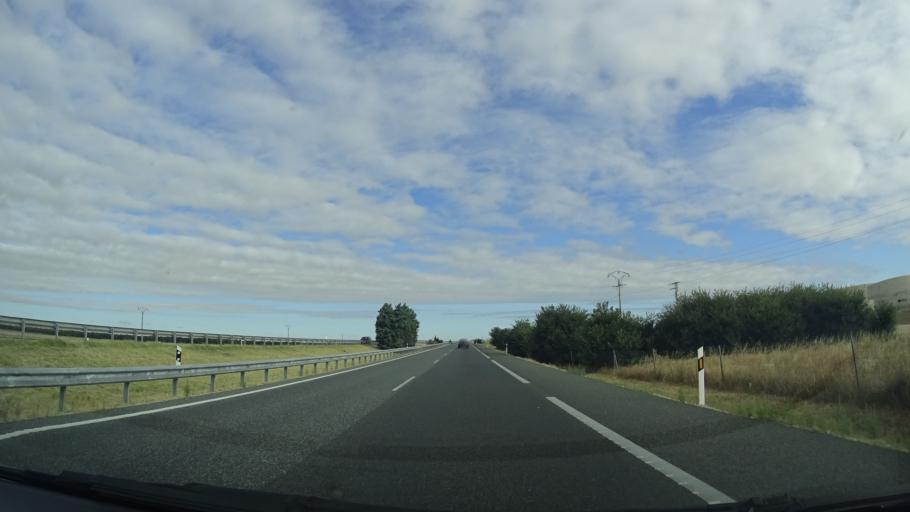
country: ES
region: Castille and Leon
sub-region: Provincia de Valladolid
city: San Vicente del Palacio
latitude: 41.2569
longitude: -4.8751
